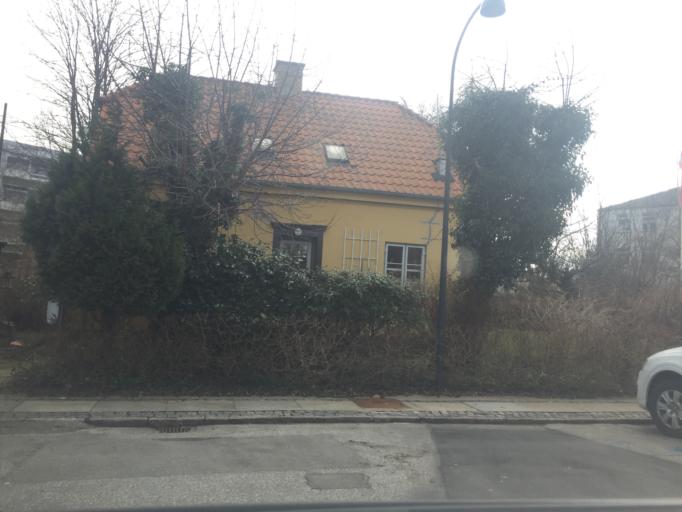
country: DK
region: Capital Region
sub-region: Gentofte Kommune
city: Charlottenlund
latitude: 55.7231
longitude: 12.5609
